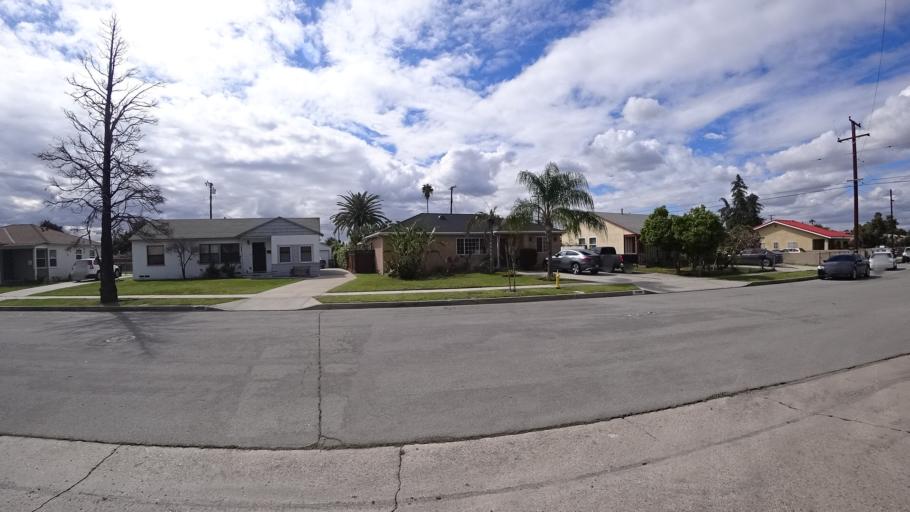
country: US
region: California
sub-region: Los Angeles County
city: Baldwin Park
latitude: 34.0940
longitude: -117.9568
